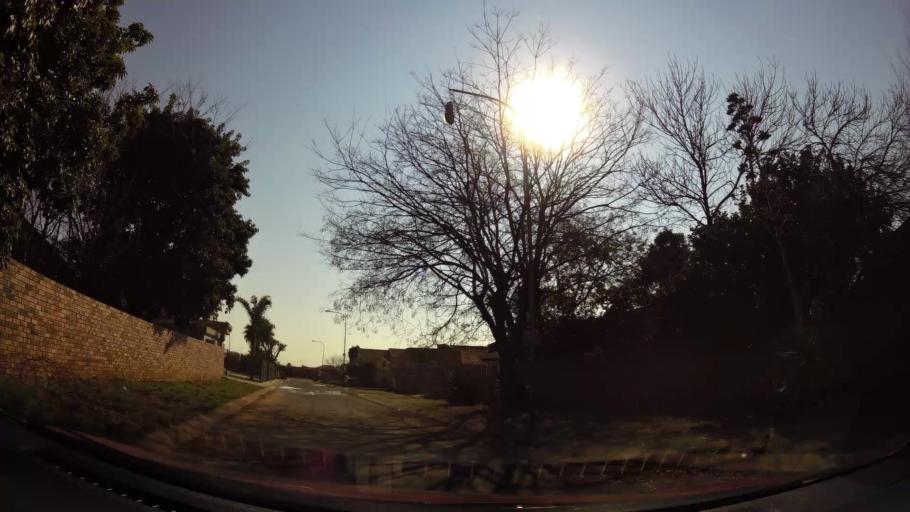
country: ZA
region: Gauteng
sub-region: City of Johannesburg Metropolitan Municipality
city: Johannesburg
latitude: -26.2495
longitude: 27.9617
